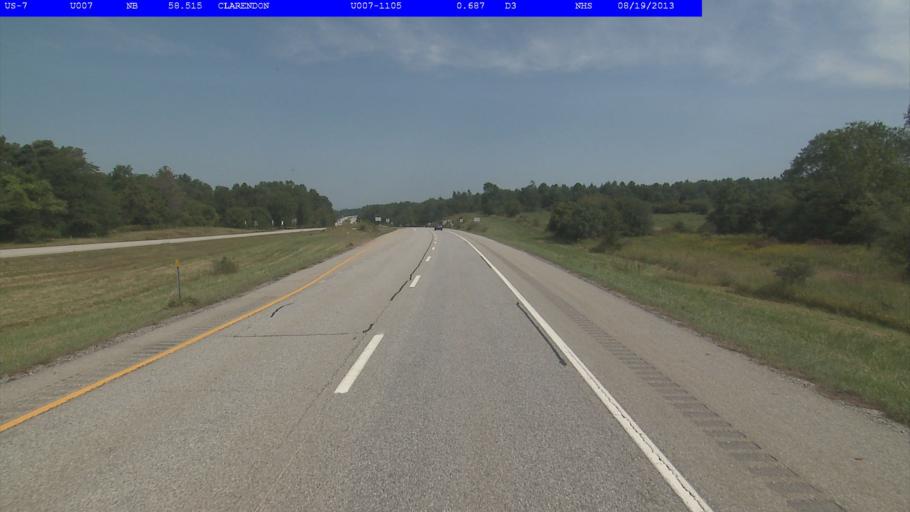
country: US
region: Vermont
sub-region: Rutland County
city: Rutland
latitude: 43.5039
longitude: -72.9671
